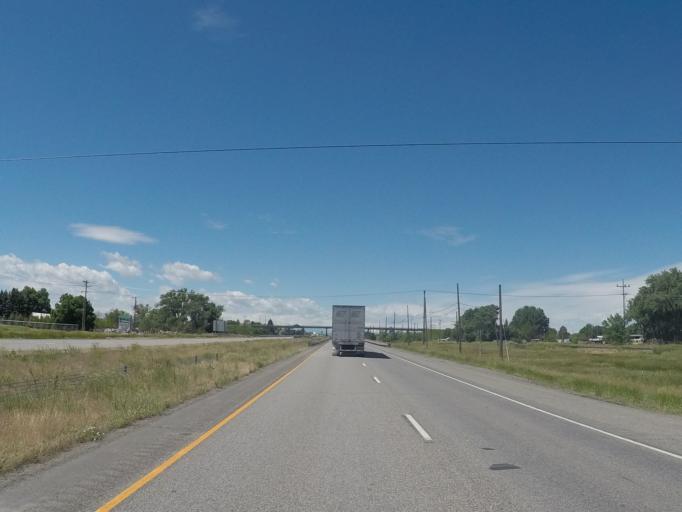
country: US
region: Montana
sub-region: Yellowstone County
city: Billings
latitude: 45.7282
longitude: -108.6125
